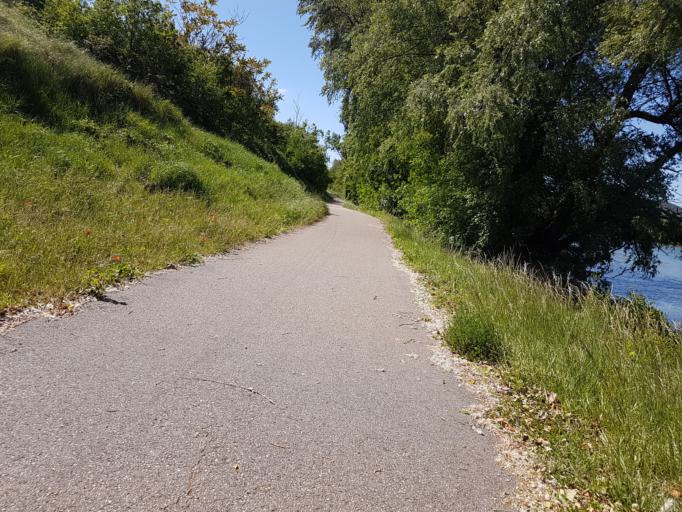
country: FR
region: Rhone-Alpes
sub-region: Departement de la Drome
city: Andancette
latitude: 45.2752
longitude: 4.8112
